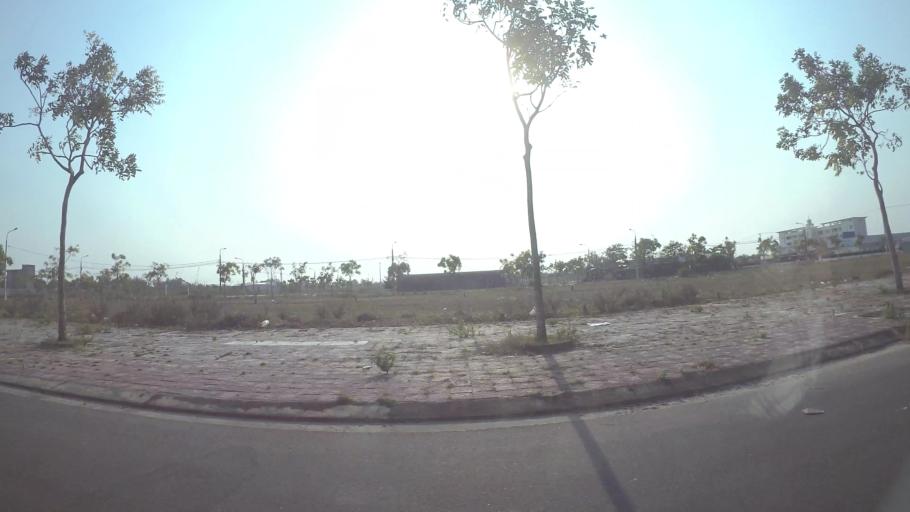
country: VN
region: Da Nang
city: Ngu Hanh Son
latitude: 15.9614
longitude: 108.2612
